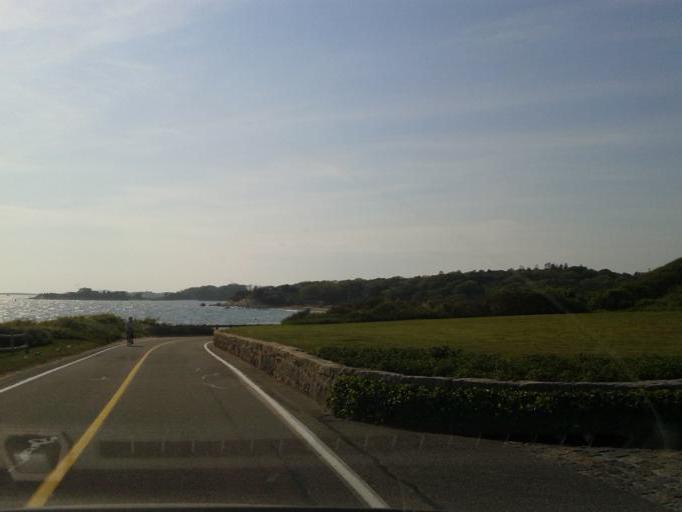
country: US
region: Massachusetts
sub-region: Barnstable County
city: Falmouth
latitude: 41.5160
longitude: -70.6564
